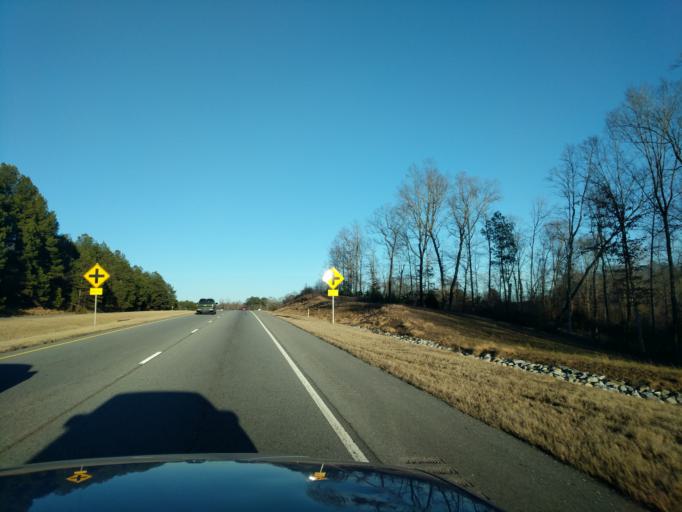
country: US
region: Georgia
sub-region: Stephens County
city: Toccoa
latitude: 34.5427
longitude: -83.2891
